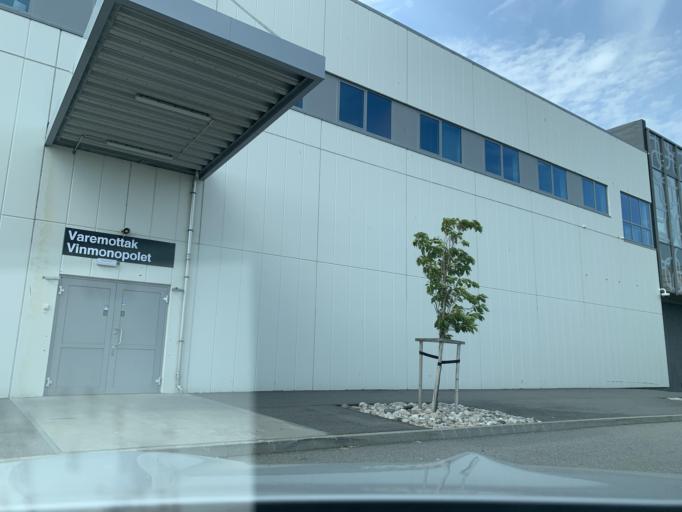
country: NO
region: Rogaland
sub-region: Klepp
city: Kleppe
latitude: 58.7793
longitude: 5.6279
